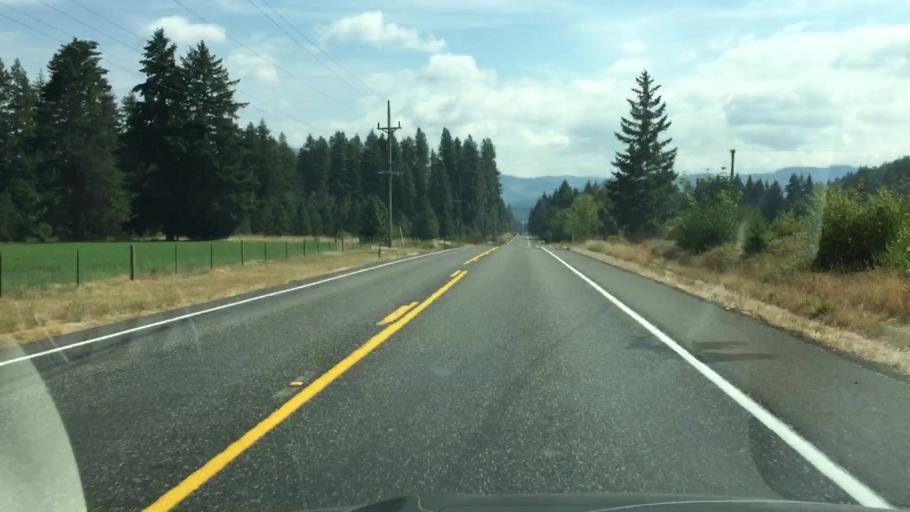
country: US
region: Washington
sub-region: Klickitat County
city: White Salmon
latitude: 45.8414
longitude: -121.5028
